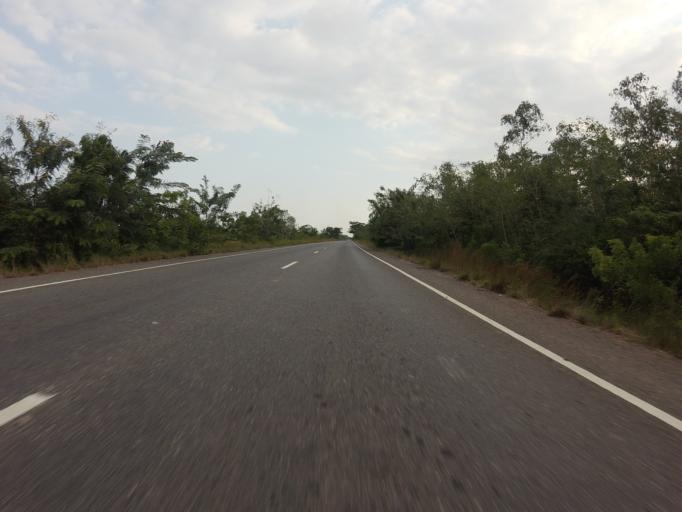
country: GH
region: Volta
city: Ho
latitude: 6.1213
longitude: 0.5207
